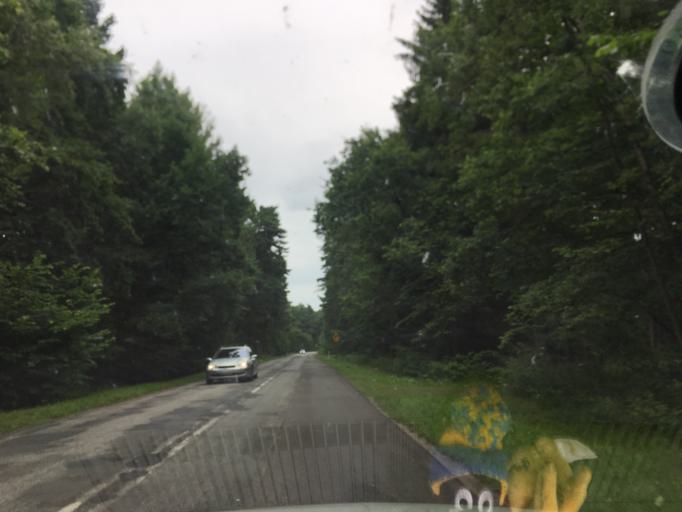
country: PL
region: West Pomeranian Voivodeship
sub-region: Powiat gryficki
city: Pobierowo
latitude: 54.0511
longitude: 14.9335
